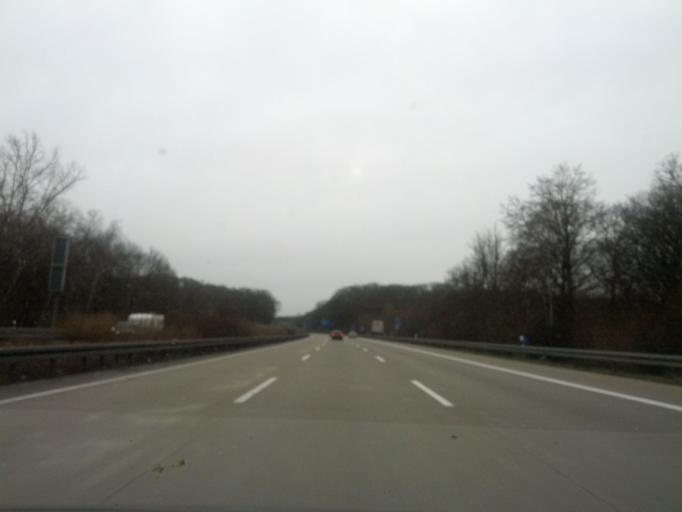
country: DE
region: Lower Saxony
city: Laatzen
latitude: 52.3182
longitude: 9.8653
